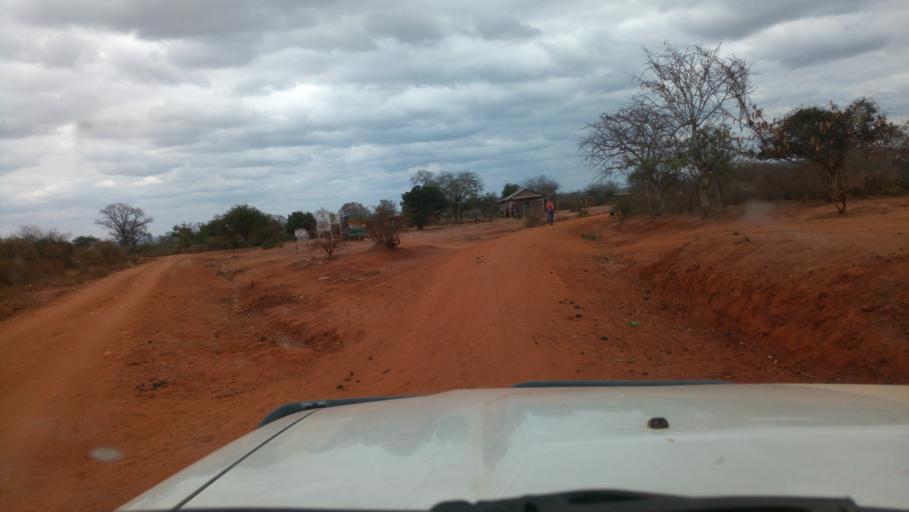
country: KE
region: Kitui
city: Kitui
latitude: -1.9362
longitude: 38.3790
